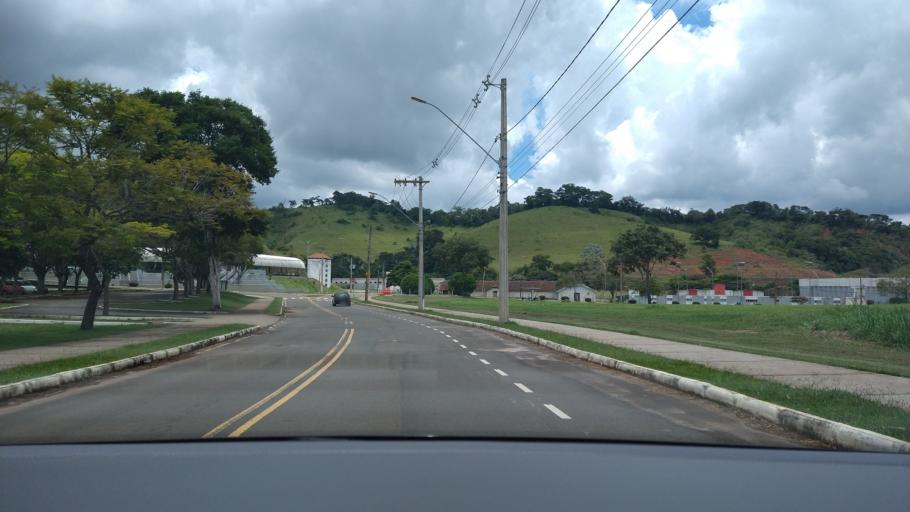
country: BR
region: Minas Gerais
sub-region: Vicosa
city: Vicosa
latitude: -20.7660
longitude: -42.8604
